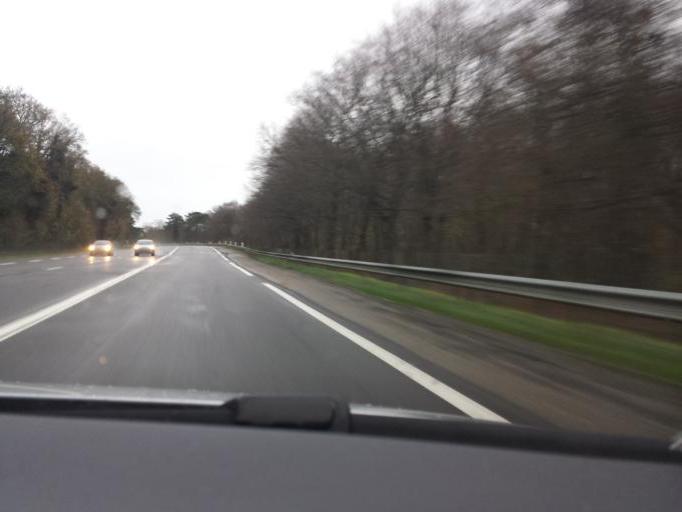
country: FR
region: Haute-Normandie
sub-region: Departement de l'Eure
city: Menilles
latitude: 49.0113
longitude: 1.3342
